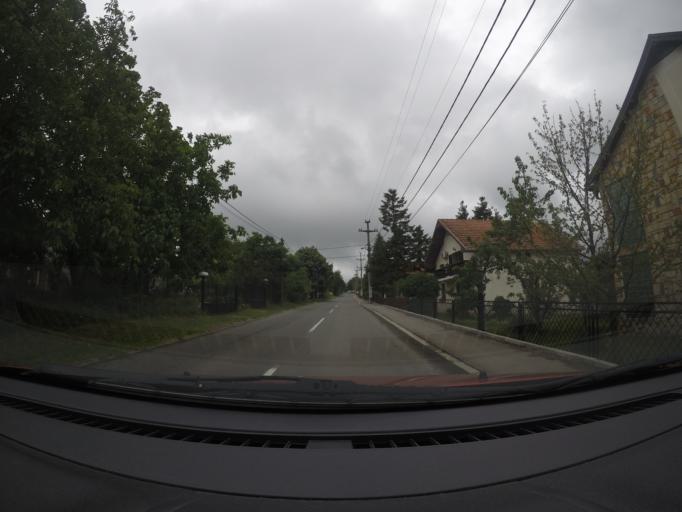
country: RS
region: Central Serbia
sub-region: Belgrade
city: Zvezdara
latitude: 44.6898
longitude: 20.5517
